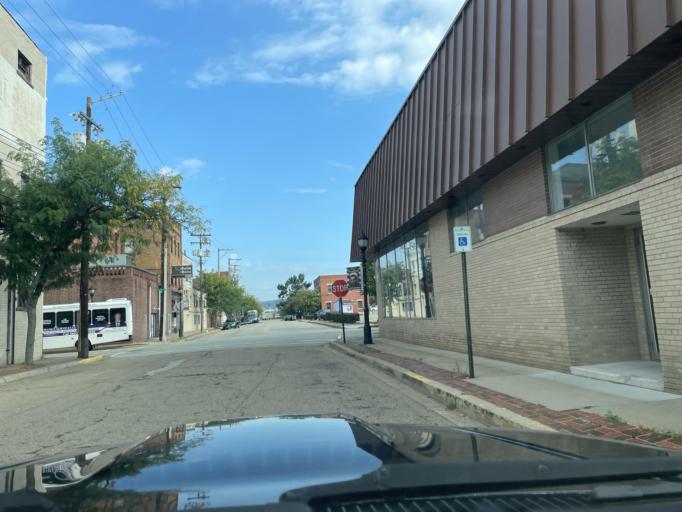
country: US
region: Pennsylvania
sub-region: Westmoreland County
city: New Kensington
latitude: 40.5652
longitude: -79.7645
